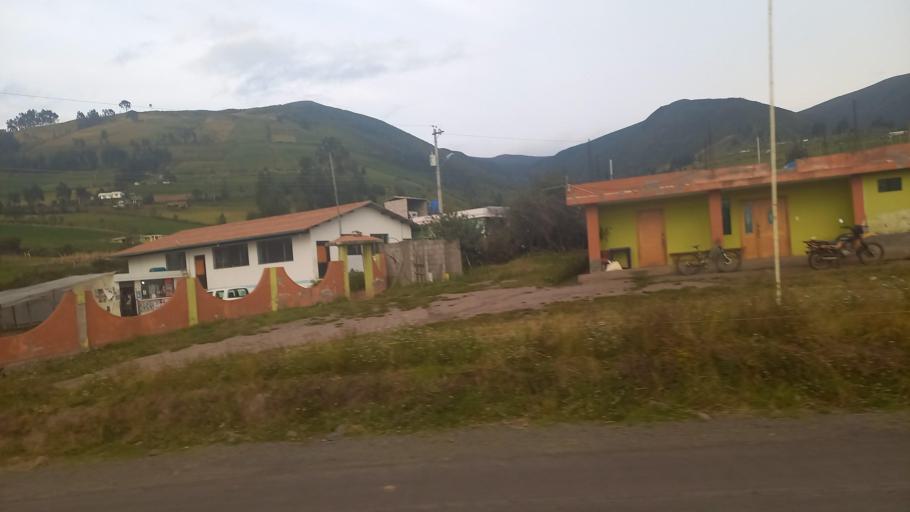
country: EC
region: Pichincha
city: Cayambe
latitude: 0.1134
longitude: -78.0781
